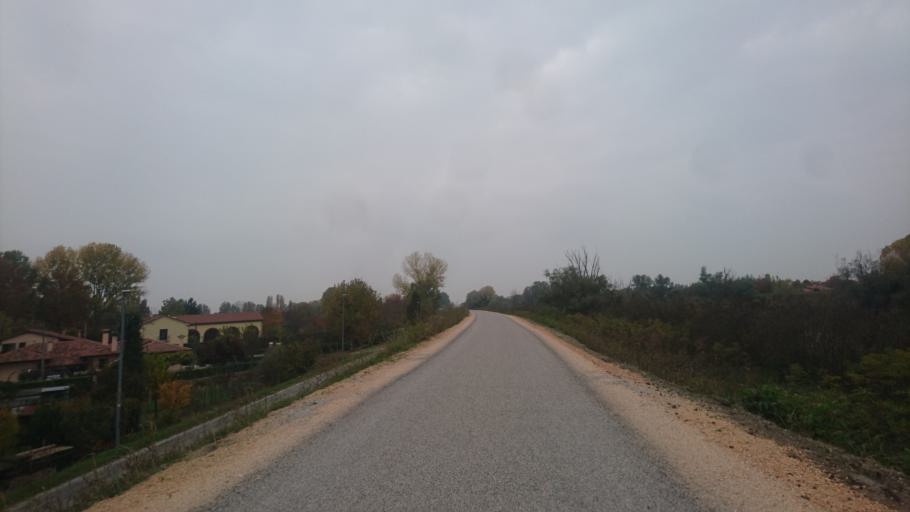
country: IT
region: Veneto
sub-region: Provincia di Padova
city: Oltre Brenta
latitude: 45.4111
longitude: 11.9941
